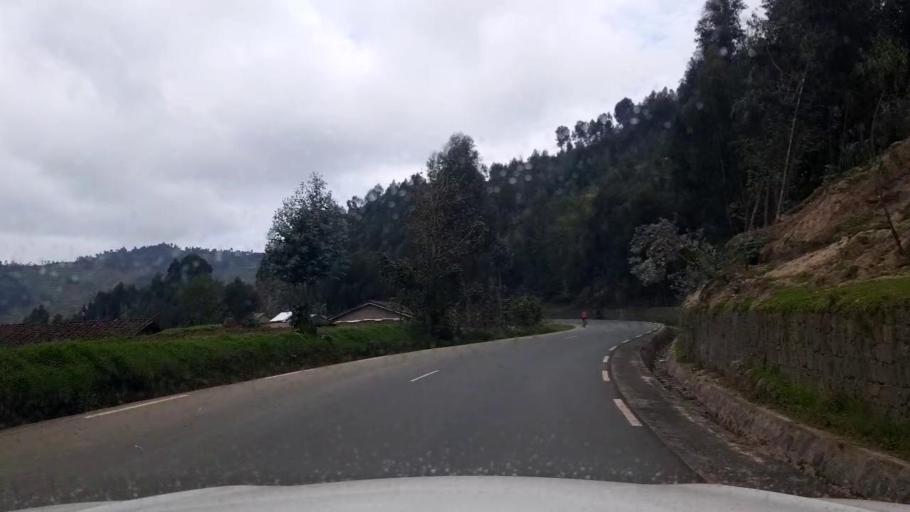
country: RW
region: Northern Province
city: Musanze
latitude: -1.6639
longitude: 29.5134
